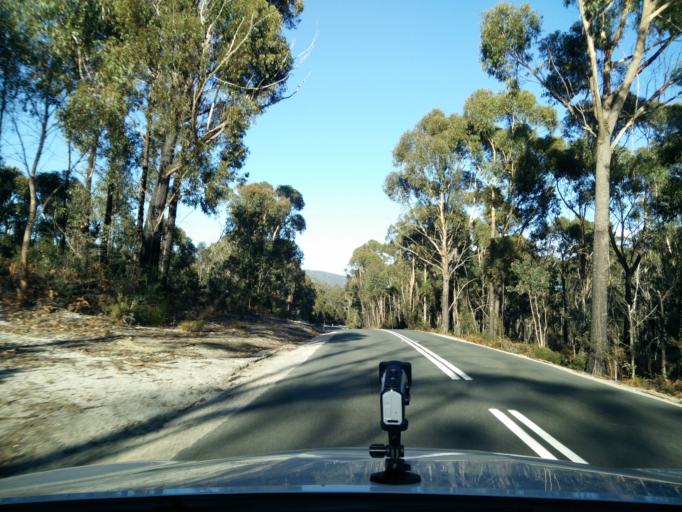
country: AU
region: Tasmania
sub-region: Break O'Day
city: St Helens
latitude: -41.2848
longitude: 148.1633
